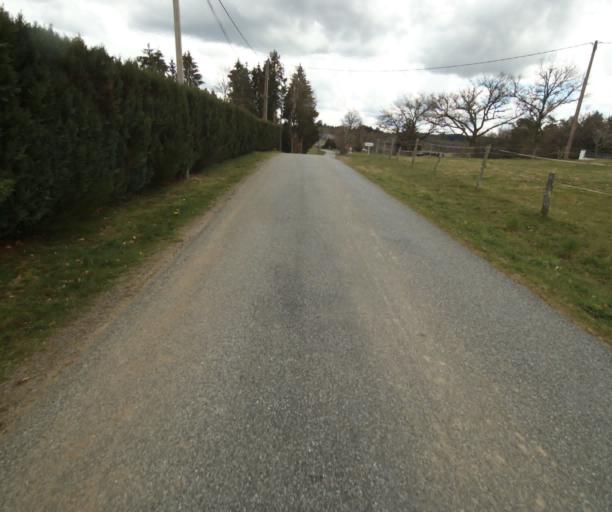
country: FR
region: Limousin
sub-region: Departement de la Correze
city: Correze
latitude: 45.3184
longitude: 1.9240
